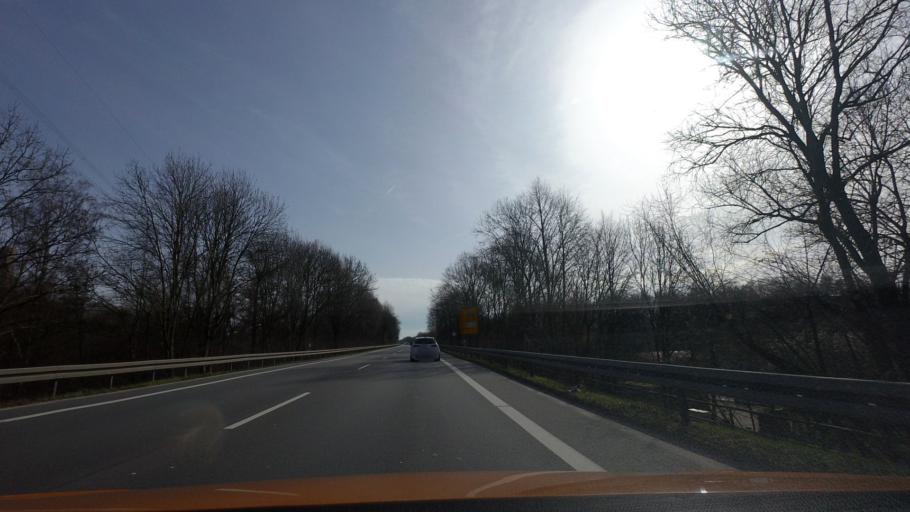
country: DE
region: North Rhine-Westphalia
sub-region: Regierungsbezirk Detmold
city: Petershagen
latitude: 52.3783
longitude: 8.9903
